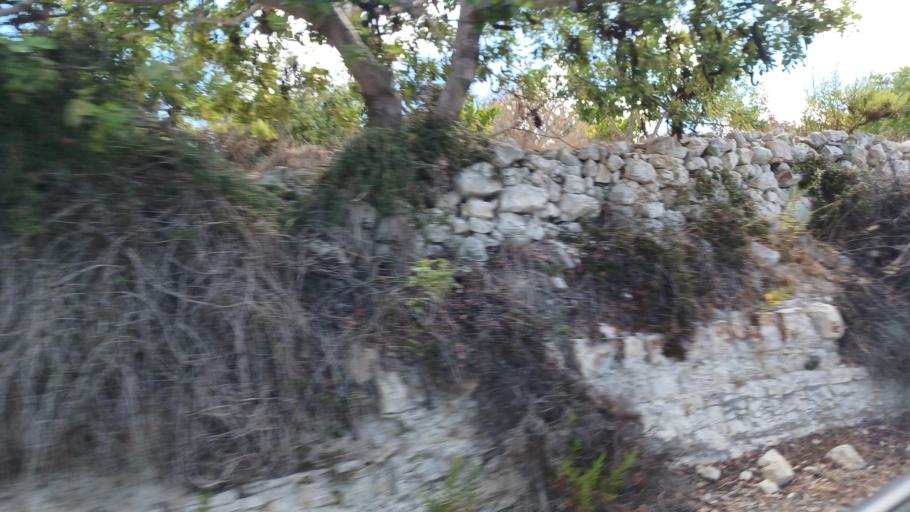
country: CY
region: Pafos
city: Tala
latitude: 34.8580
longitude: 32.4425
